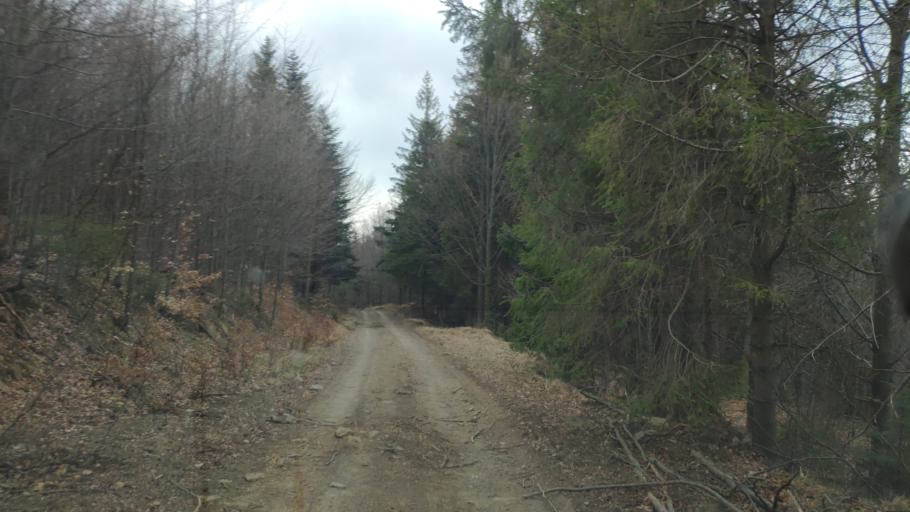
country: SK
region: Kosicky
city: Gelnica
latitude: 48.7554
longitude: 21.0398
